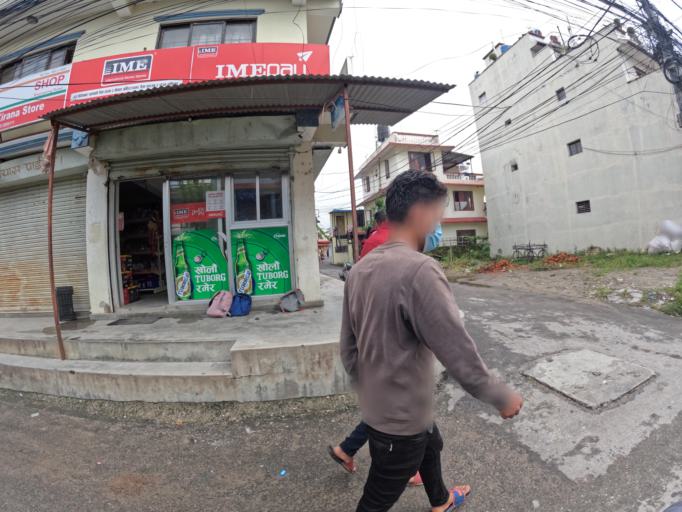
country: NP
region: Central Region
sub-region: Bagmati Zone
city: Kathmandu
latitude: 27.7513
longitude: 85.3233
